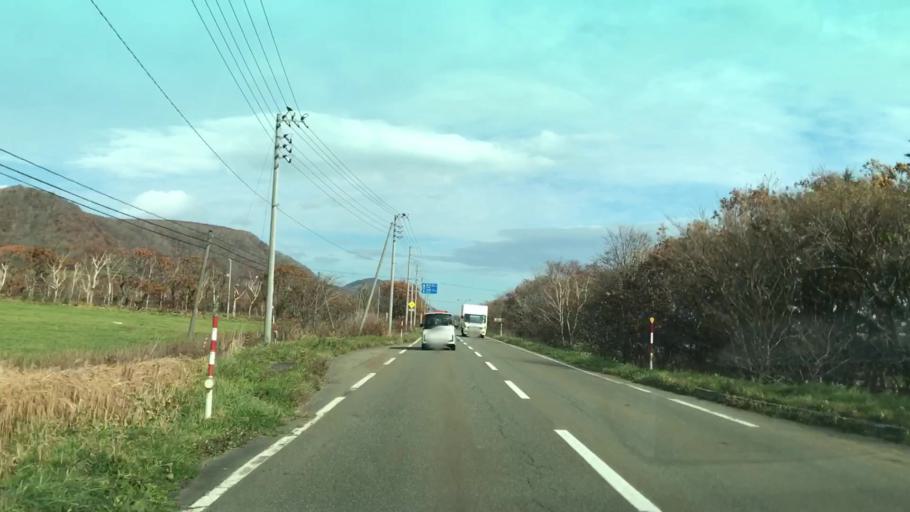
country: JP
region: Hokkaido
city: Obihiro
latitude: 42.0190
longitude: 143.2566
